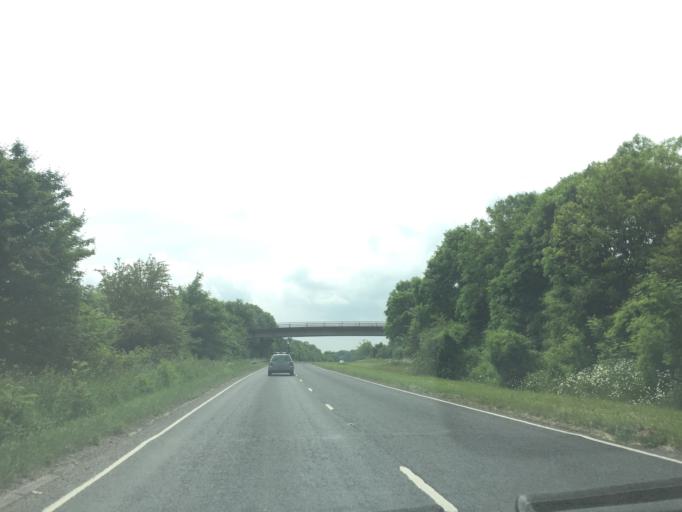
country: GB
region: England
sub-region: Hampshire
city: Alton
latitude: 51.1537
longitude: -0.9517
